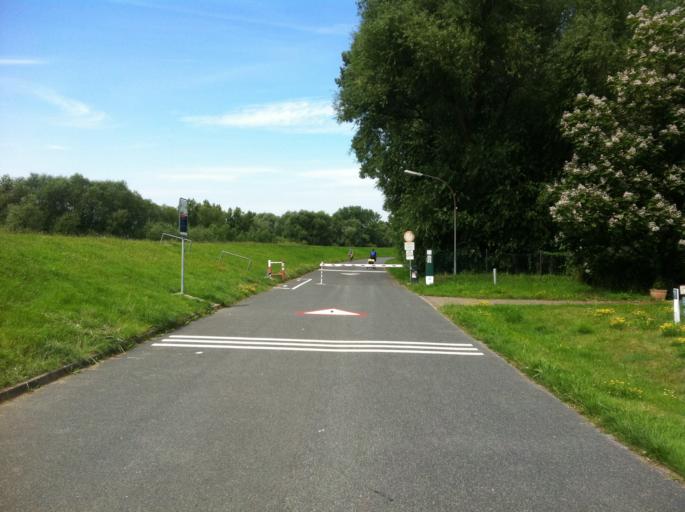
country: DE
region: Hamburg
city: Rothenburgsort
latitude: 53.5008
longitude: 10.0721
